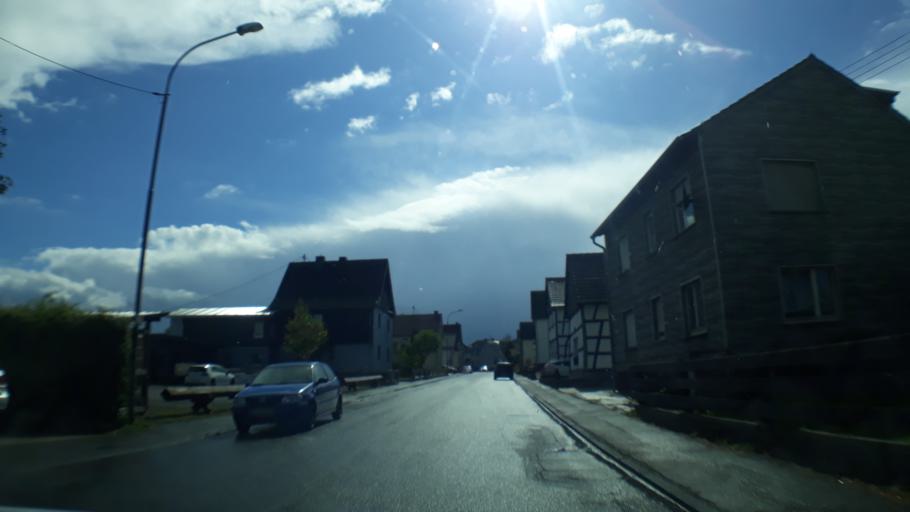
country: DE
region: North Rhine-Westphalia
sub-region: Regierungsbezirk Koln
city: Schleiden
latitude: 50.4955
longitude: 6.5214
